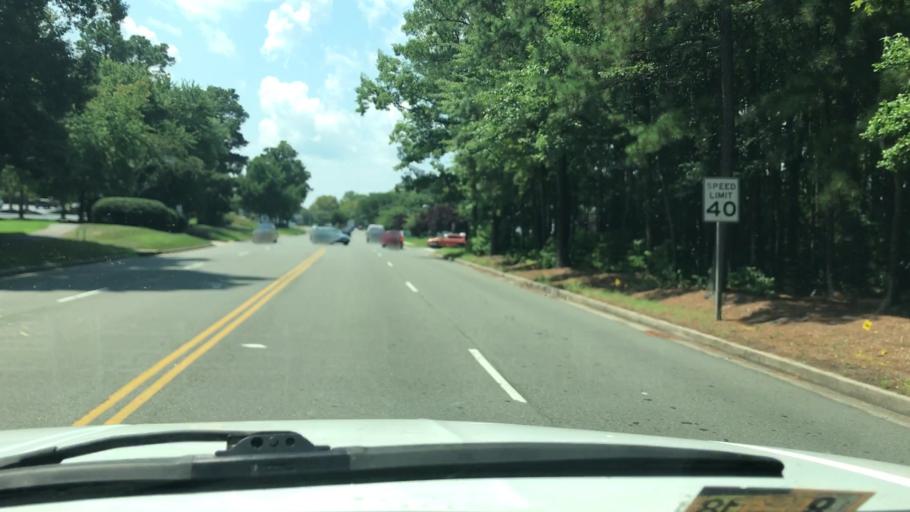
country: US
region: Virginia
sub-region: Henrico County
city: Short Pump
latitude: 37.6507
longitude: -77.5856
